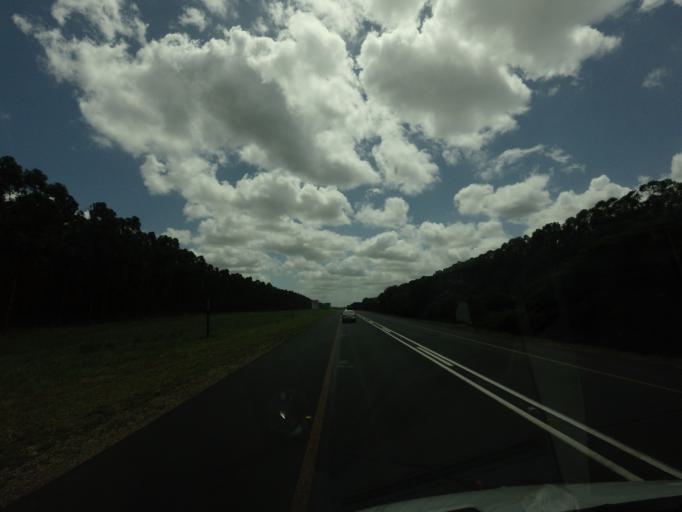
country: ZA
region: KwaZulu-Natal
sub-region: uThungulu District Municipality
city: KwaMbonambi
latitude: -28.5350
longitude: 32.1319
